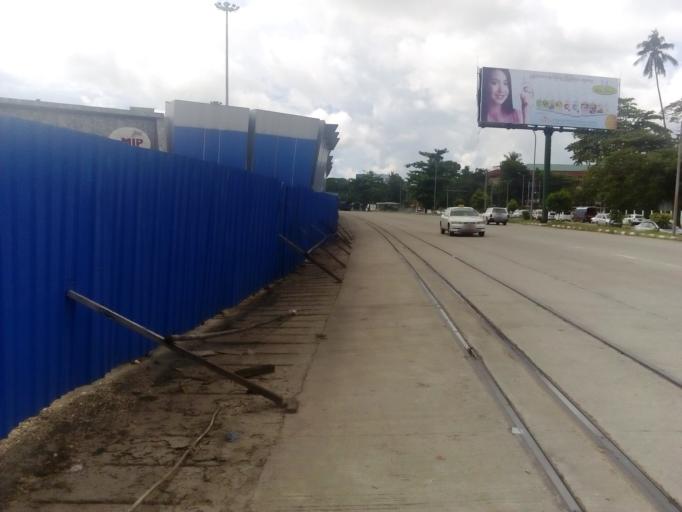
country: MM
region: Yangon
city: Yangon
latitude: 16.7784
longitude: 96.1351
